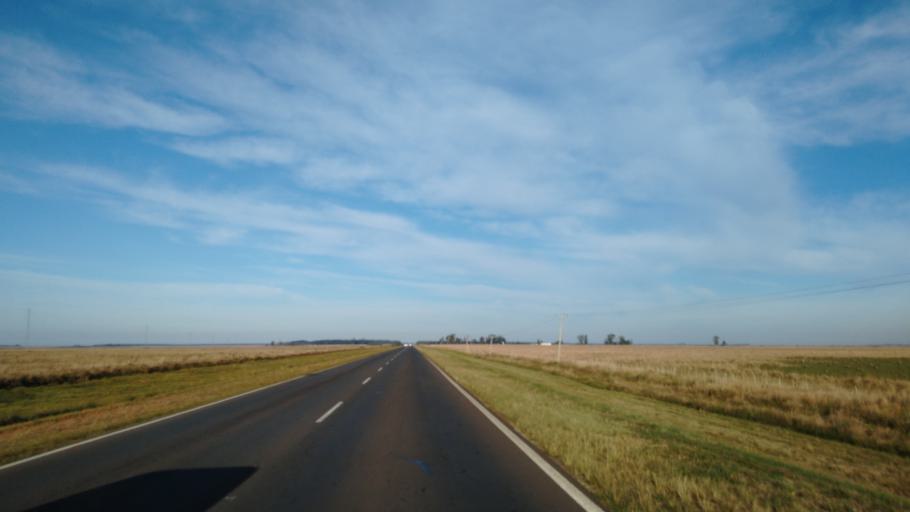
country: AR
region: Corrientes
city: La Cruz
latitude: -29.2278
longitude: -56.7180
